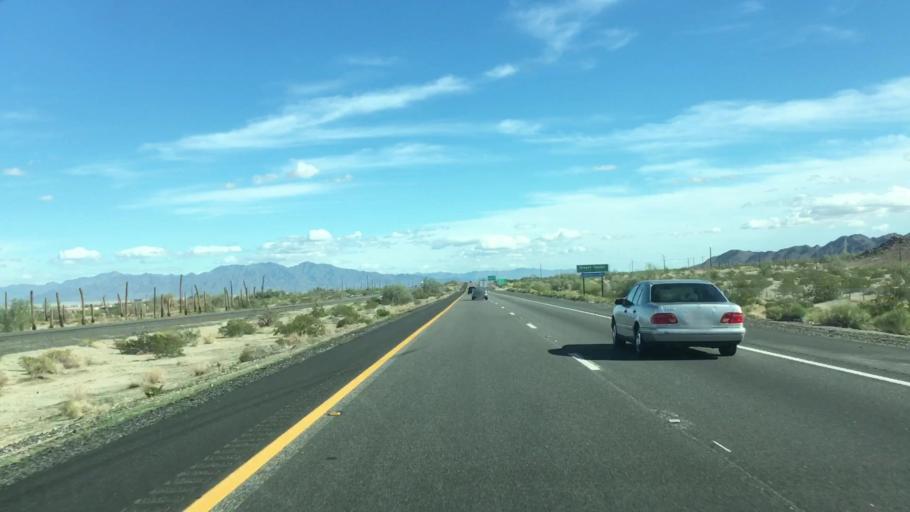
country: US
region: California
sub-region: Imperial County
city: Niland
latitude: 33.7103
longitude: -115.4106
